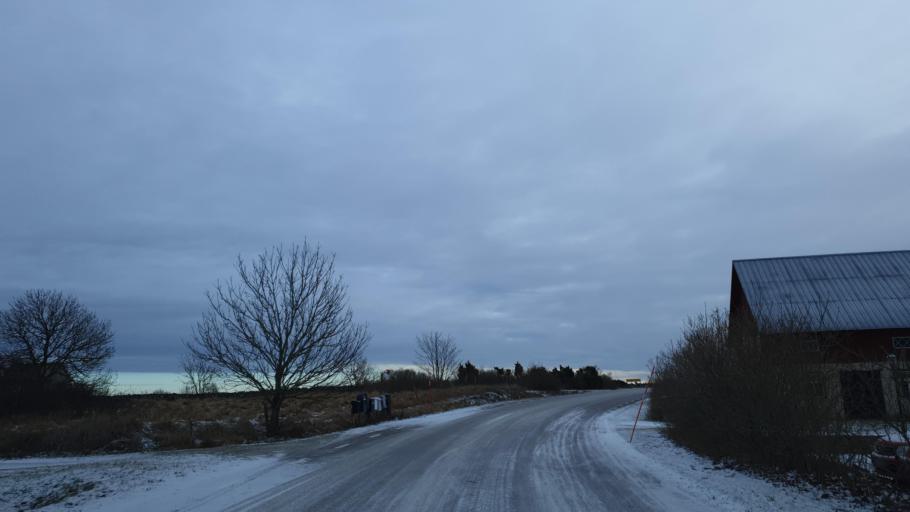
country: SE
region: Gotland
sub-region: Gotland
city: Slite
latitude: 57.4220
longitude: 18.9070
